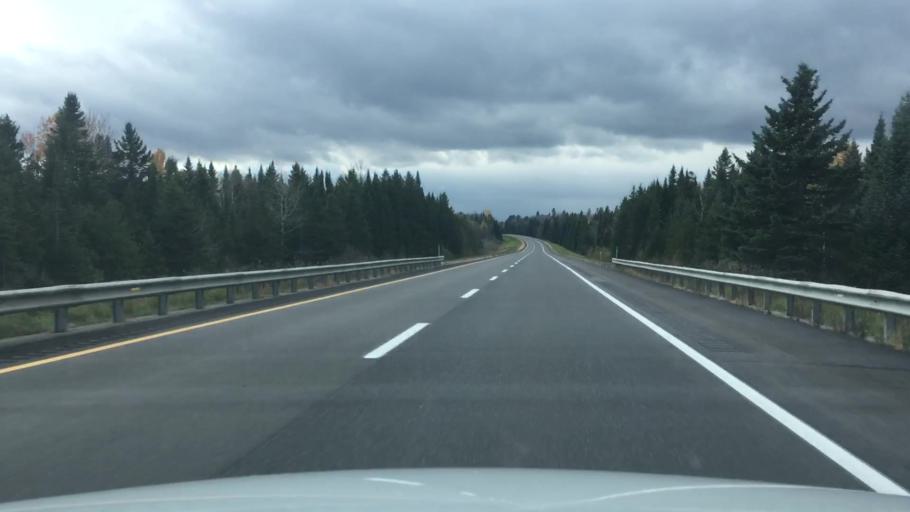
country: US
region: Maine
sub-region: Penobscot County
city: Patten
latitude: 46.0945
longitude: -68.1948
